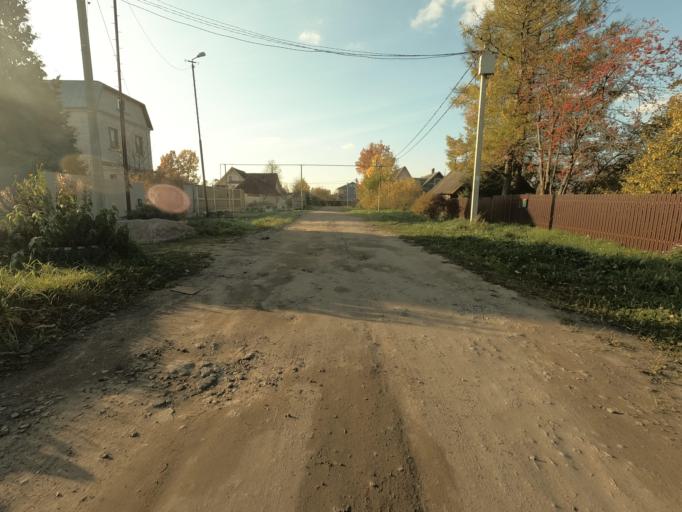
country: RU
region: Leningrad
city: Mga
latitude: 59.7539
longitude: 31.0522
